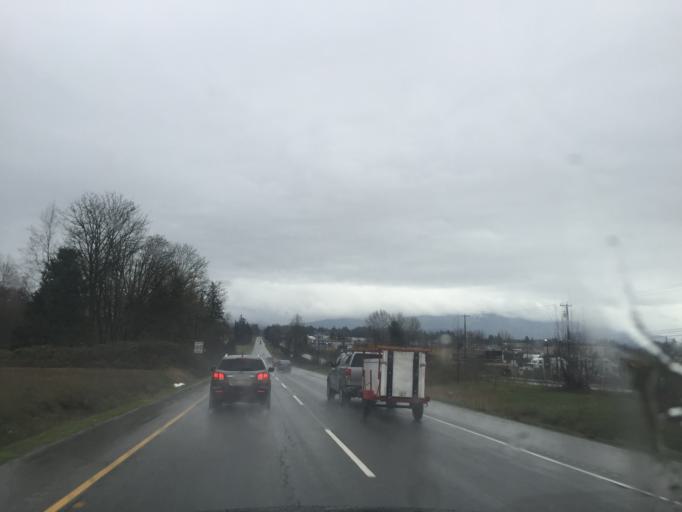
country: CA
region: British Columbia
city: Aldergrove
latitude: 49.0527
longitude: -122.3699
